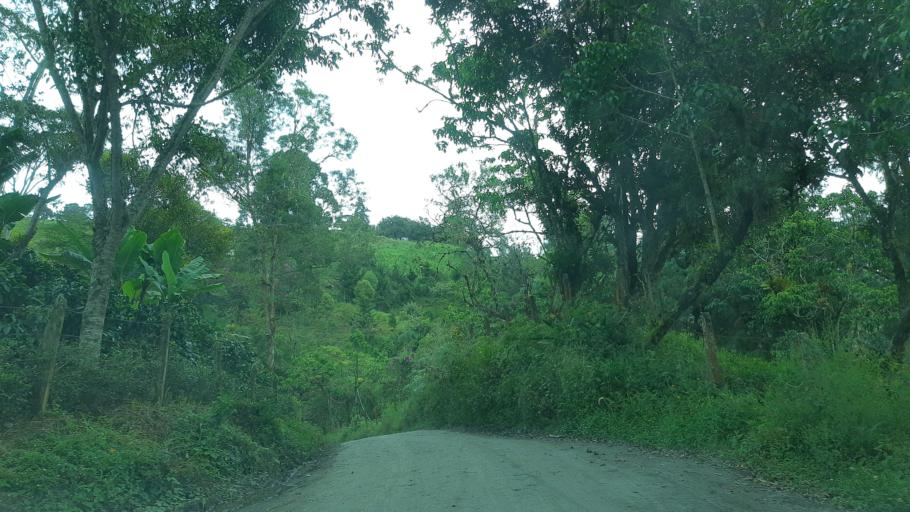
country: CO
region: Boyaca
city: Chivor
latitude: 4.9768
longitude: -73.3203
